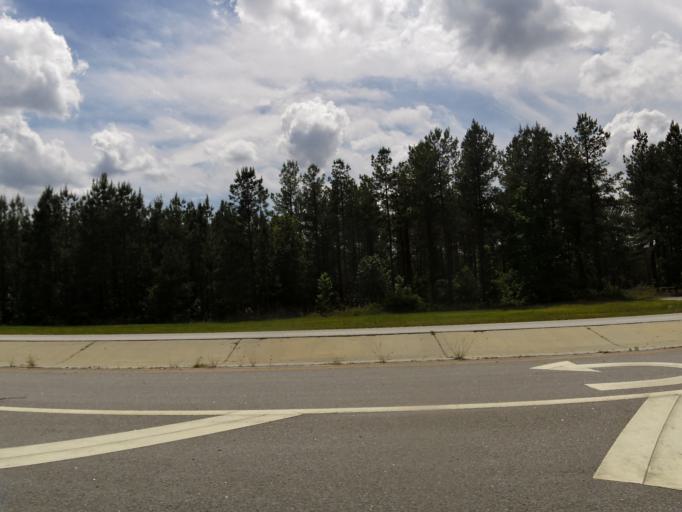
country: US
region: Georgia
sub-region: Jefferson County
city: Wadley
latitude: 32.7751
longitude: -82.3844
